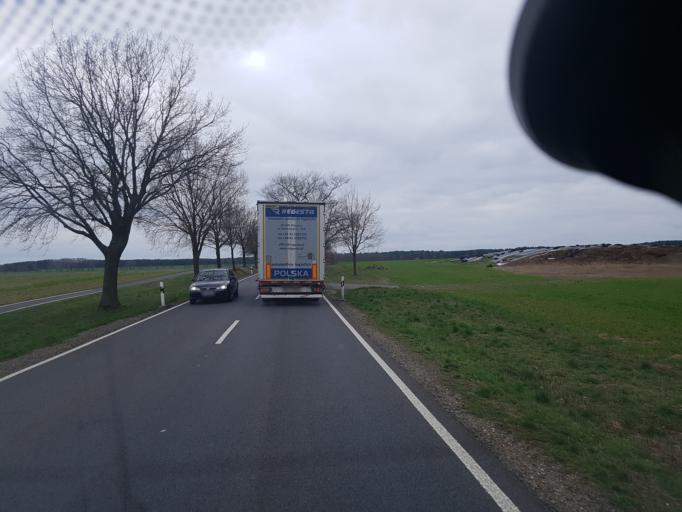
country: DE
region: Brandenburg
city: Tauche
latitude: 52.0784
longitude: 14.1596
